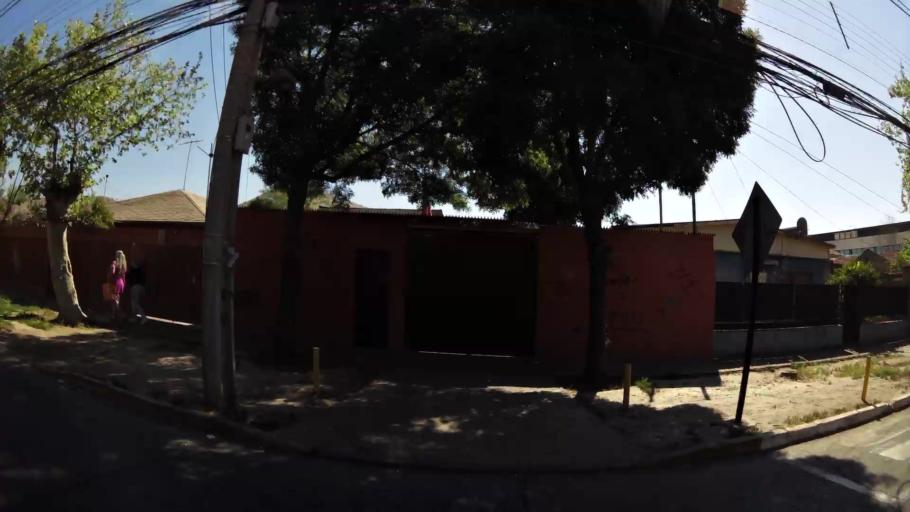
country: CL
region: Santiago Metropolitan
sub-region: Provincia de Maipo
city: San Bernardo
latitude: -33.5951
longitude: -70.7108
